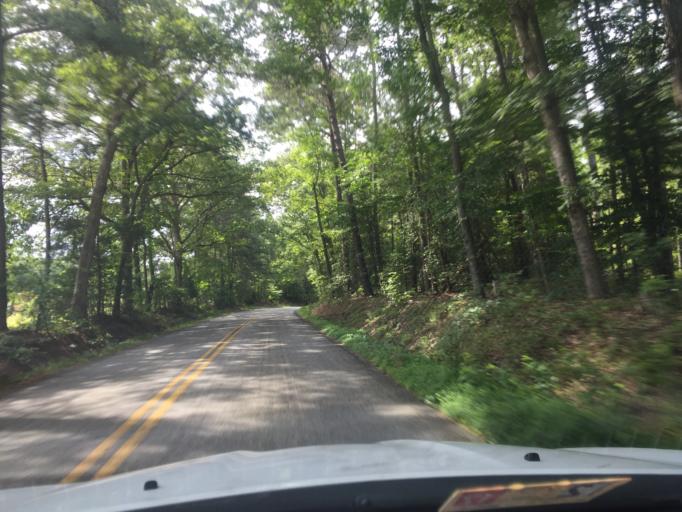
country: US
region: Virginia
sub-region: Charles City County
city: Charles City
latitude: 37.3968
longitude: -77.0171
